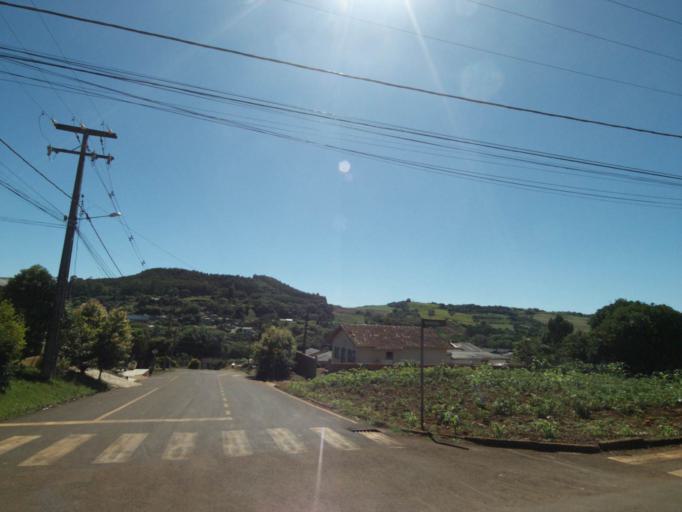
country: BR
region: Santa Catarina
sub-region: Sao Lourenco Do Oeste
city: Sao Lourenco dOeste
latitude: -26.2716
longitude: -52.7795
